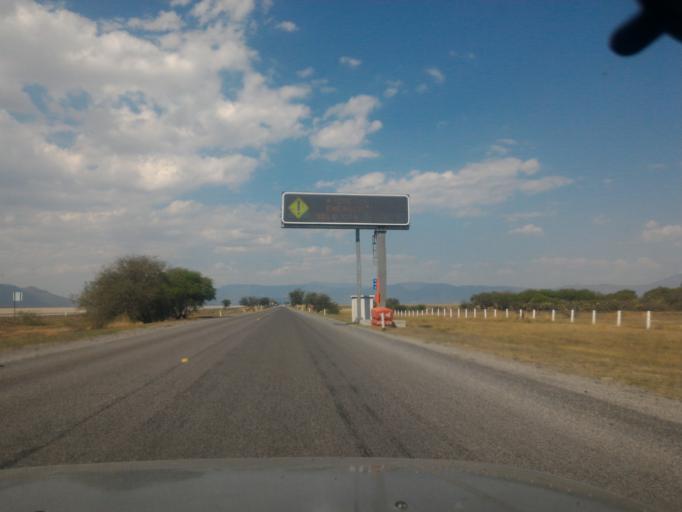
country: MX
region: Jalisco
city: Atoyac
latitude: 20.0317
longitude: -103.5286
